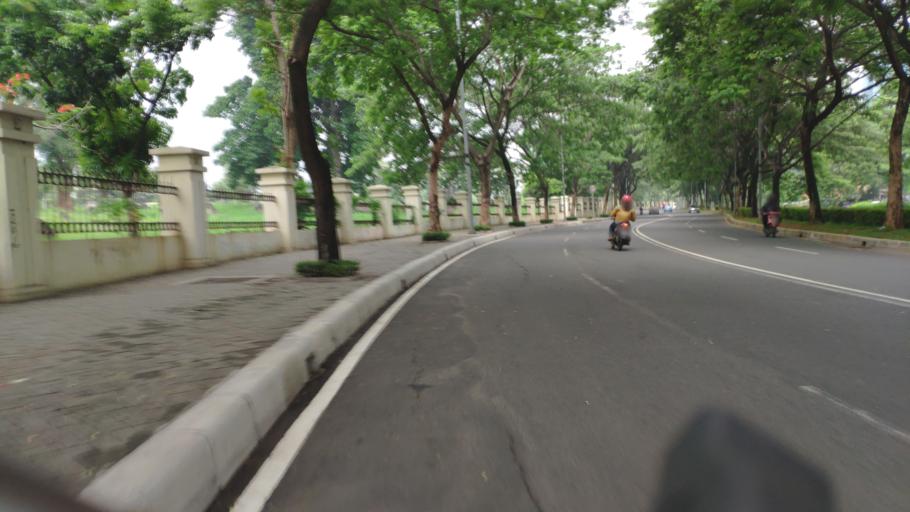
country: ID
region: Jakarta Raya
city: Jakarta
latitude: -6.2217
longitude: 106.8361
